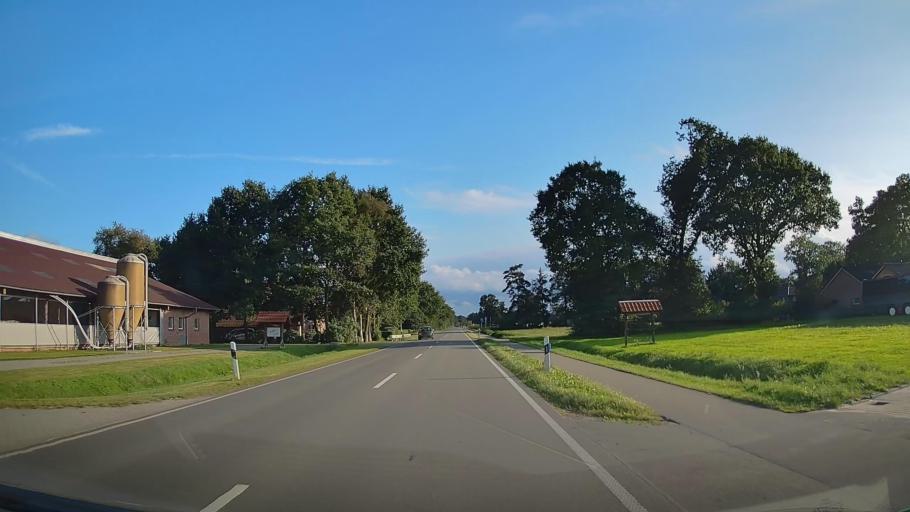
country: DE
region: Lower Saxony
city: Barssel
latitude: 53.1025
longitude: 7.7097
